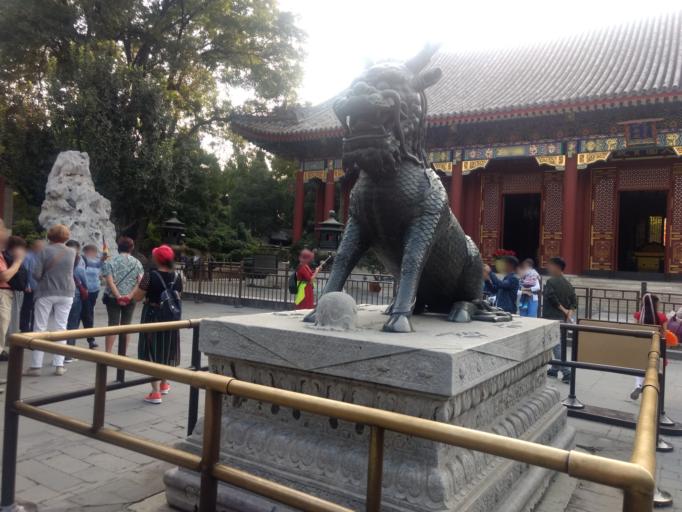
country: CN
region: Beijing
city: Haidian
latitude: 39.9966
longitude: 116.2744
